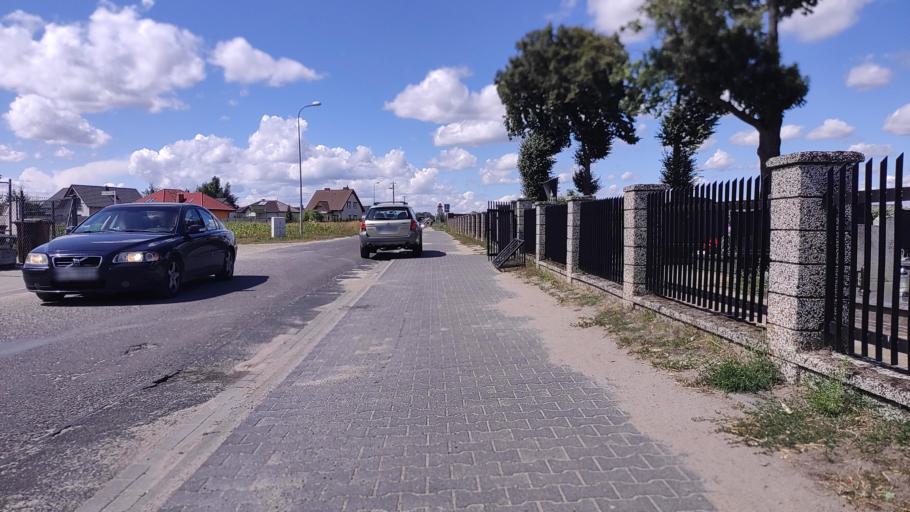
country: PL
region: Greater Poland Voivodeship
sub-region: Powiat poznanski
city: Kleszczewo
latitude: 52.3826
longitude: 17.1582
